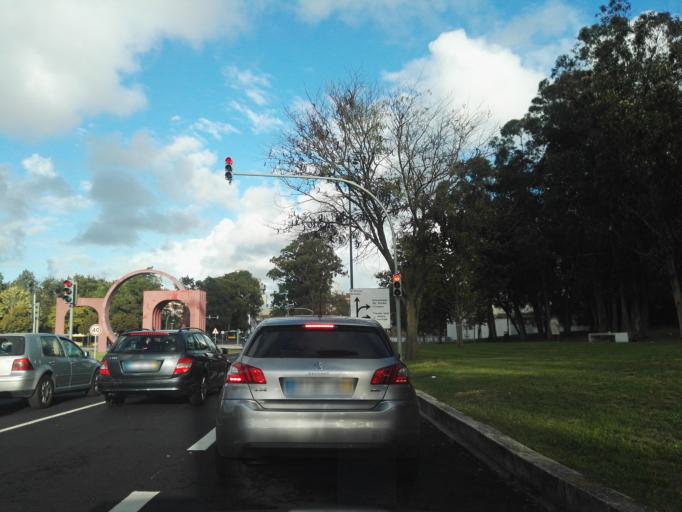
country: PT
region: Lisbon
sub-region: Odivelas
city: Olival do Basto
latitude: 38.7538
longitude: -9.1541
